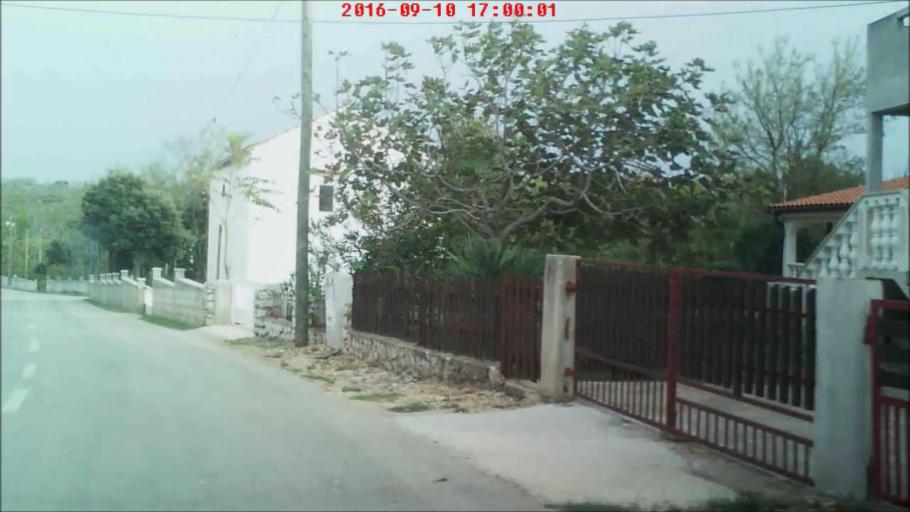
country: HR
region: Zadarska
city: Vir
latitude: 44.3107
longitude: 15.0557
